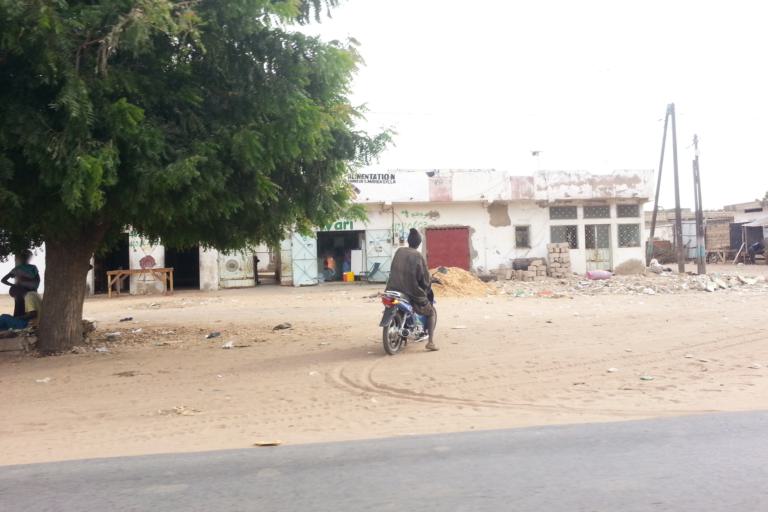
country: SN
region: Diourbel
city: Touba
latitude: 14.8801
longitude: -15.8954
